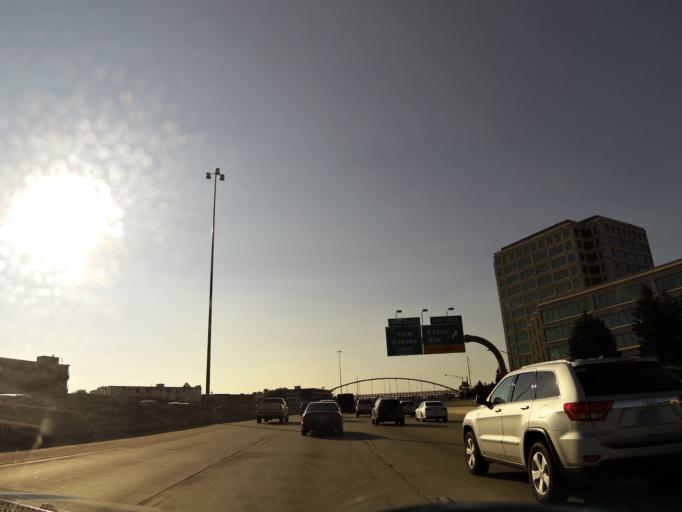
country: US
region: Colorado
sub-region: Arapahoe County
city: Glendale
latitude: 39.6816
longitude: -104.9377
